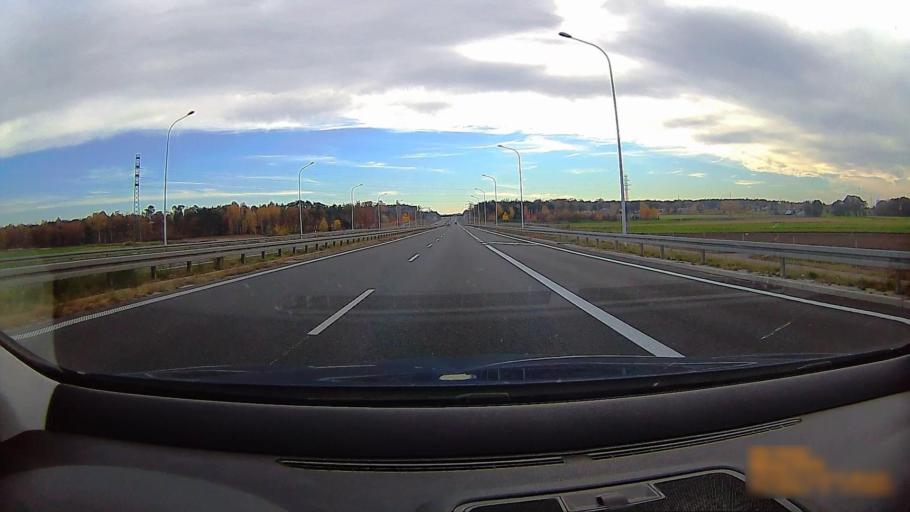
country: PL
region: Greater Poland Voivodeship
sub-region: Powiat ostrowski
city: Ostrow Wielkopolski
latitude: 51.6624
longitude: 17.8586
